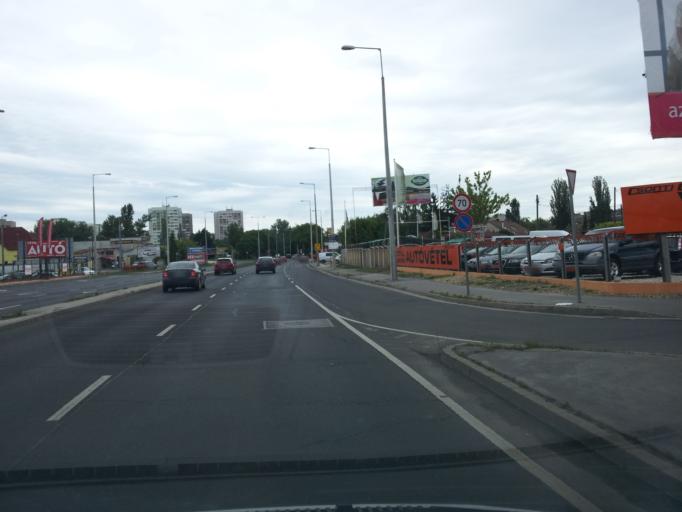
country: HU
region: Pest
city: Budakalasz
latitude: 47.5900
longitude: 19.0506
